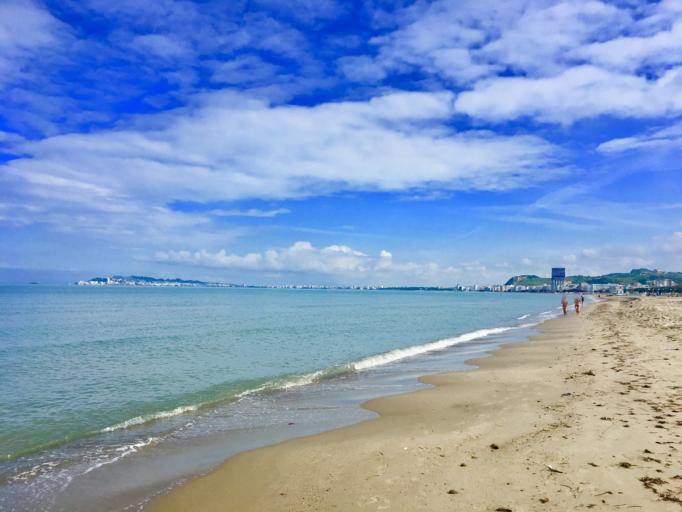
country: AL
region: Tirane
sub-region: Rrethi i Kavajes
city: Golem
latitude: 41.2483
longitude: 19.5188
